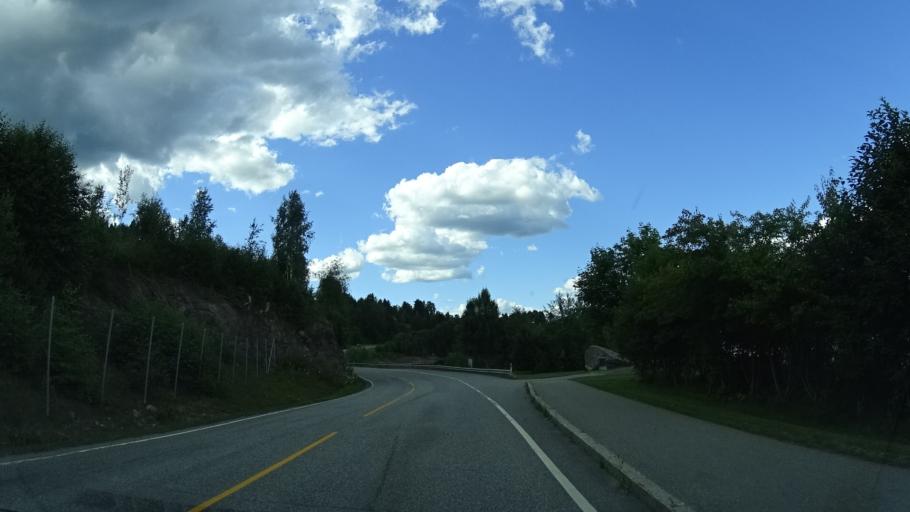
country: NO
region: Ostfold
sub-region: Marker
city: Orje
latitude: 59.4867
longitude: 11.6417
